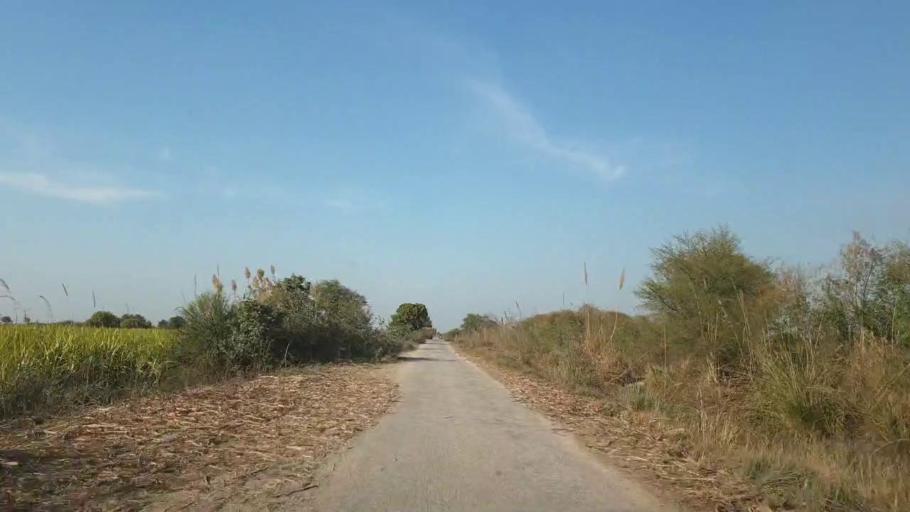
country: PK
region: Sindh
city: Tando Adam
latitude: 25.7223
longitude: 68.7030
